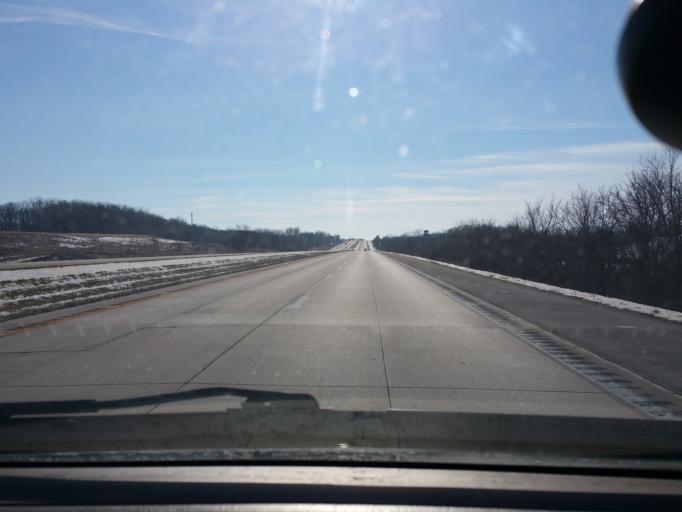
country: US
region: Missouri
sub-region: Daviess County
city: Gallatin
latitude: 39.9913
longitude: -94.0955
